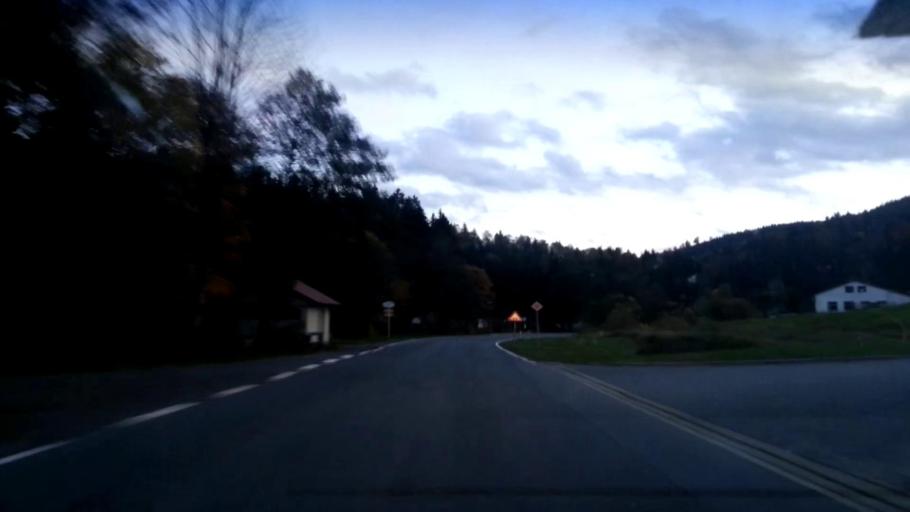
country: DE
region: Bavaria
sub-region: Upper Franconia
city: Warmensteinach
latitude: 49.9857
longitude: 11.7713
